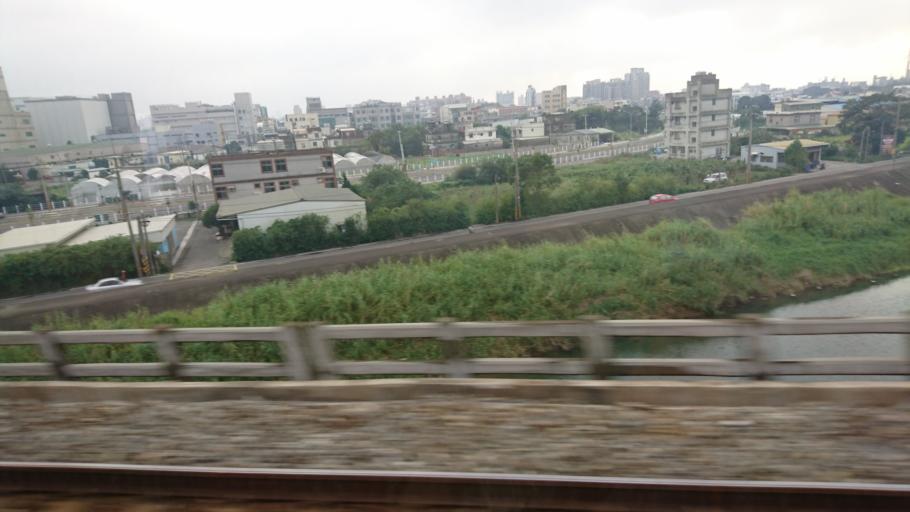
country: TW
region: Taiwan
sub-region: Hsinchu
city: Zhubei
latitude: 24.8514
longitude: 121.0127
